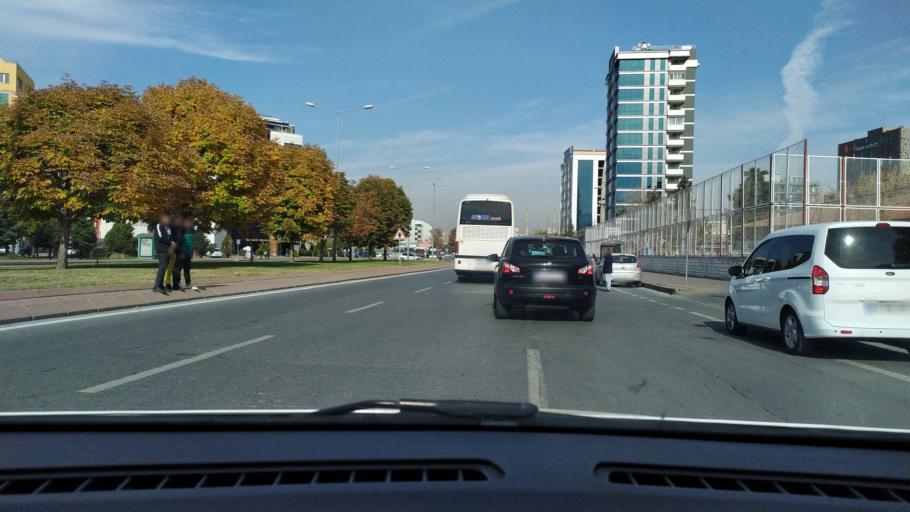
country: TR
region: Kayseri
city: Kayseri
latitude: 38.7113
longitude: 35.4911
